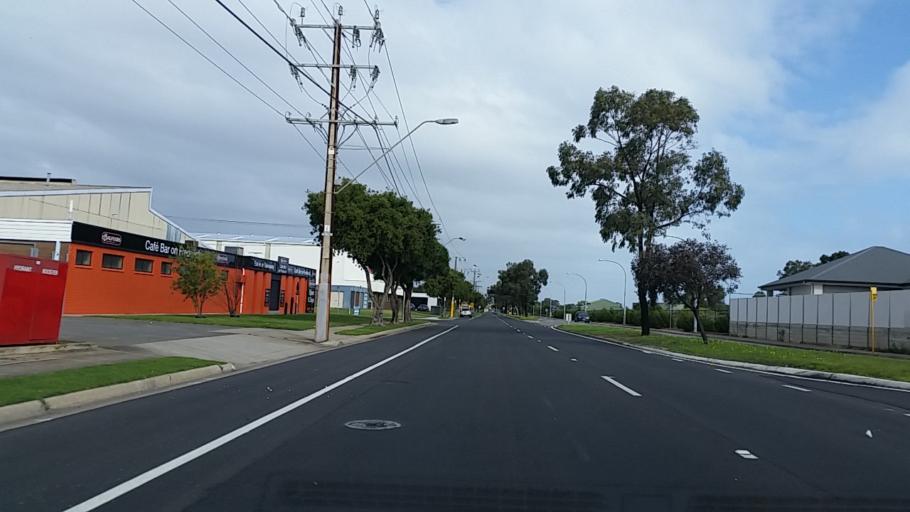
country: AU
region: South Australia
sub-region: Charles Sturt
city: Royal Park
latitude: -34.8678
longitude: 138.5030
